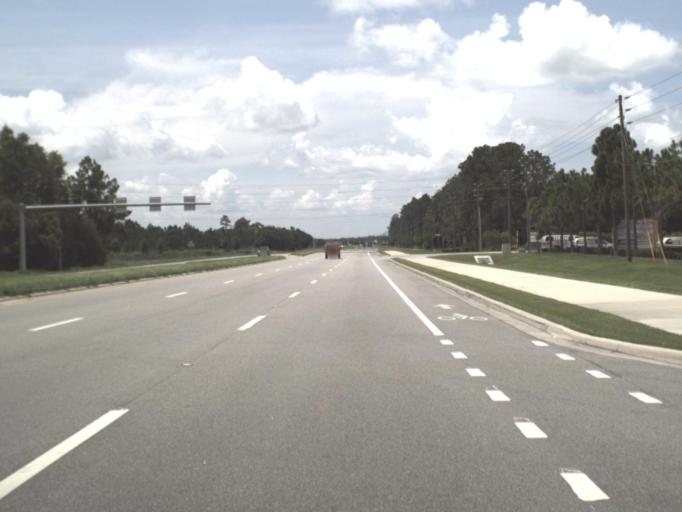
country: US
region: Florida
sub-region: Pasco County
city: Wesley Chapel
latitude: 28.2348
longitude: -82.3502
